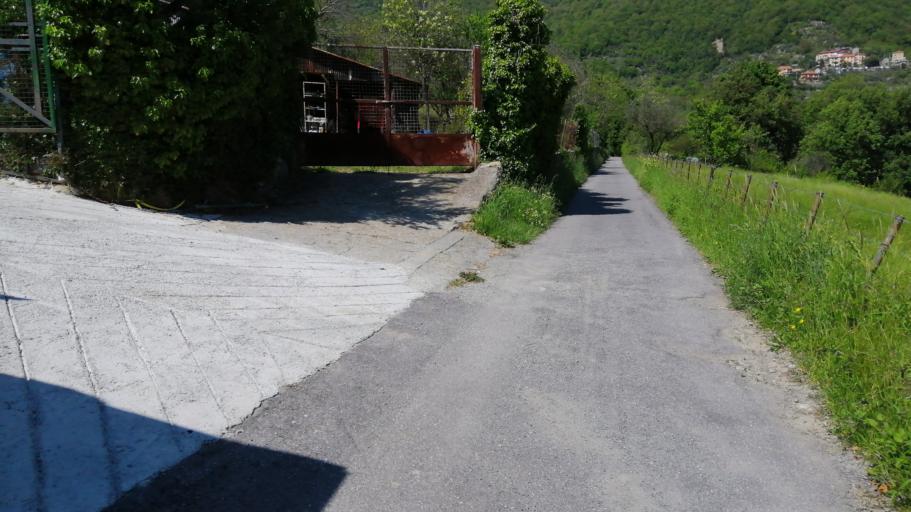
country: IT
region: Liguria
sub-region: Provincia di Genova
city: Piccarello
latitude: 44.4593
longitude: 8.9739
